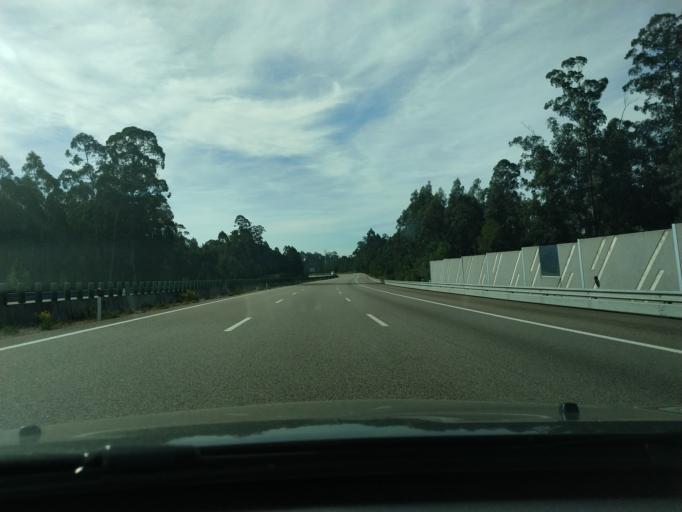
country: PT
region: Aveiro
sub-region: Ovar
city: Valega
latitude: 40.8540
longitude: -8.5558
